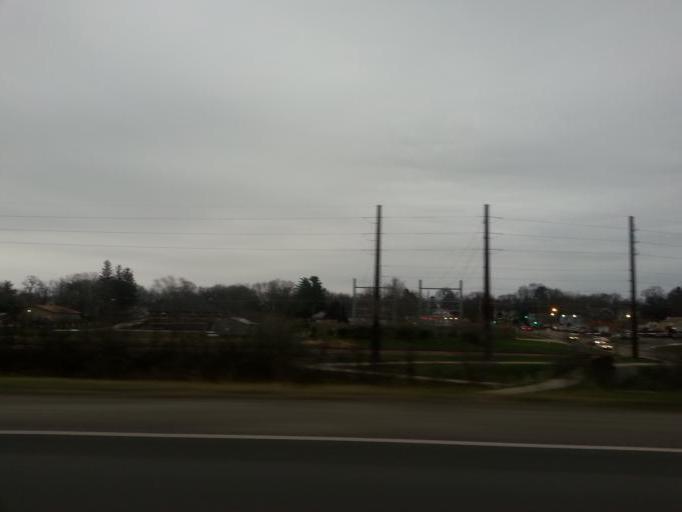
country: US
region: Iowa
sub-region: Linn County
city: Cedar Rapids
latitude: 42.0074
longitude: -91.6659
